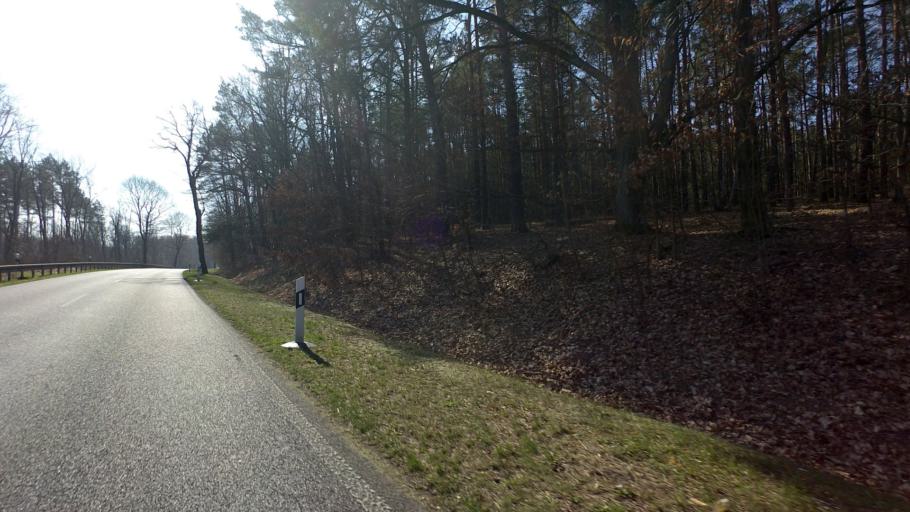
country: DE
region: Brandenburg
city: Baruth
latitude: 52.1226
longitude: 13.4829
